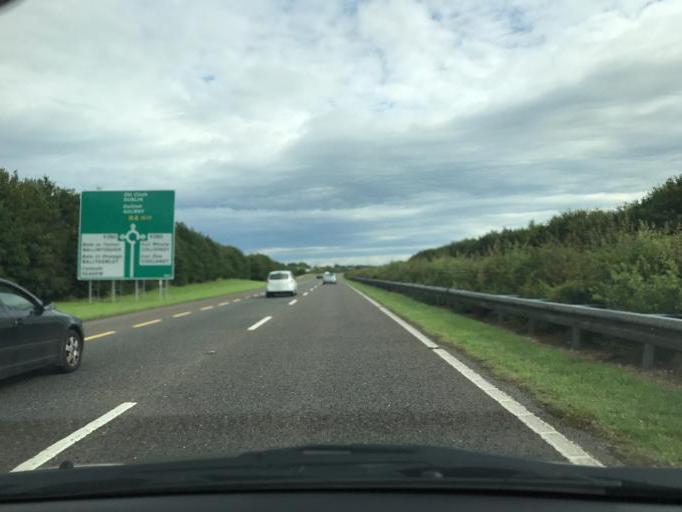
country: IE
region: Connaught
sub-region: Sligo
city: Collooney
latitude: 54.1925
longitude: -8.4920
